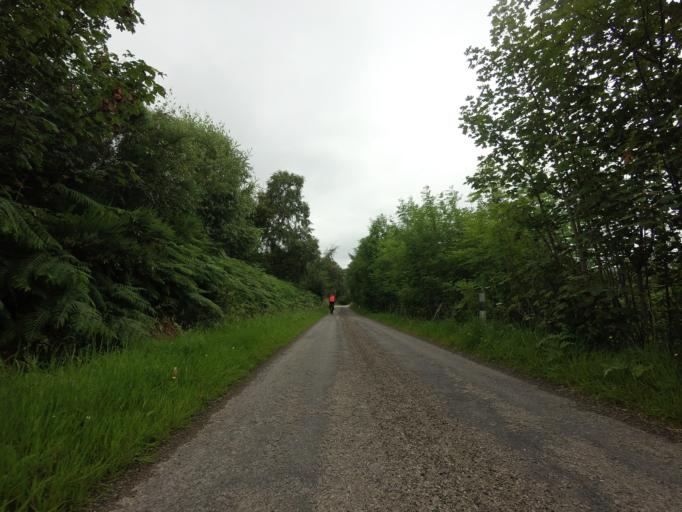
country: GB
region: Scotland
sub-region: Highland
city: Alness
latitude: 57.8945
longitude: -4.3756
